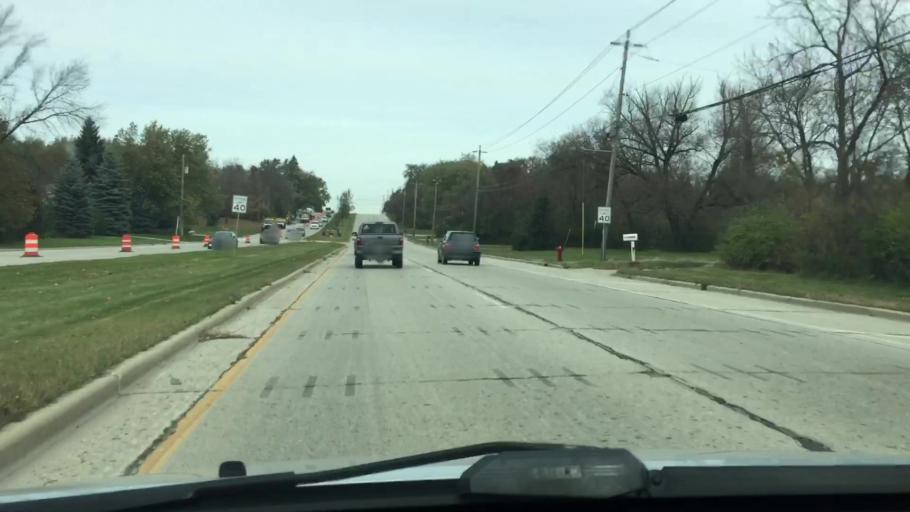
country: US
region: Wisconsin
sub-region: Waukesha County
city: New Berlin
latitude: 42.9598
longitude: -88.1089
